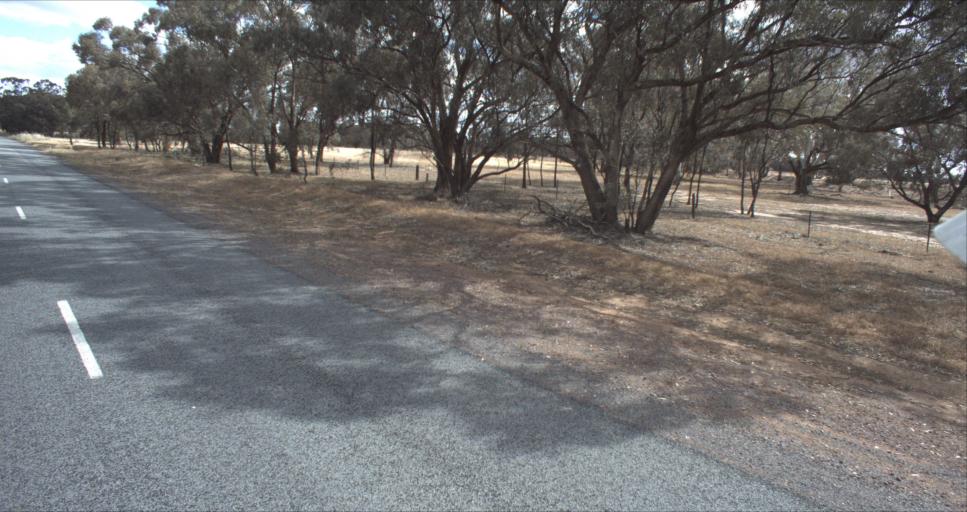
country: AU
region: New South Wales
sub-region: Leeton
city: Leeton
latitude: -34.6648
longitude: 146.3486
